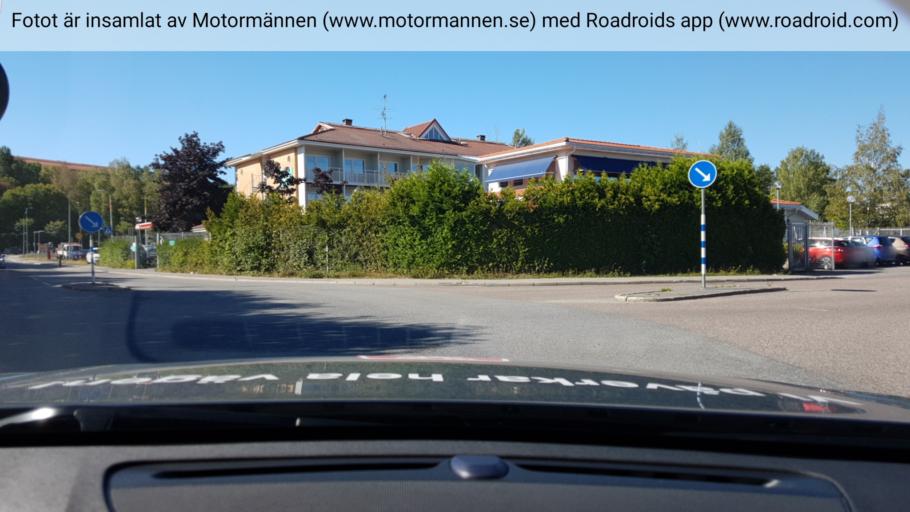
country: SE
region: Stockholm
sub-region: Tyreso Kommun
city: Bollmora
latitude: 59.2446
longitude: 18.2201
